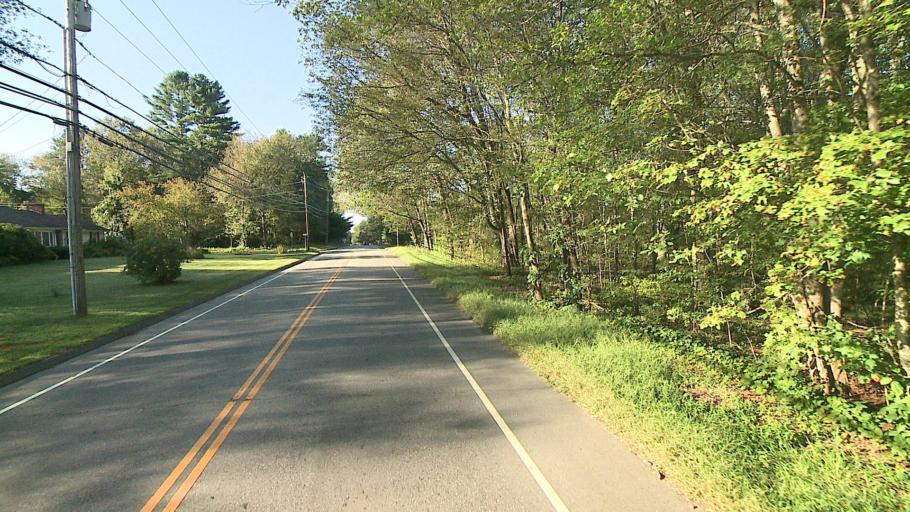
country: US
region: Connecticut
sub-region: Windham County
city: East Brooklyn
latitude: 41.7733
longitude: -71.8967
